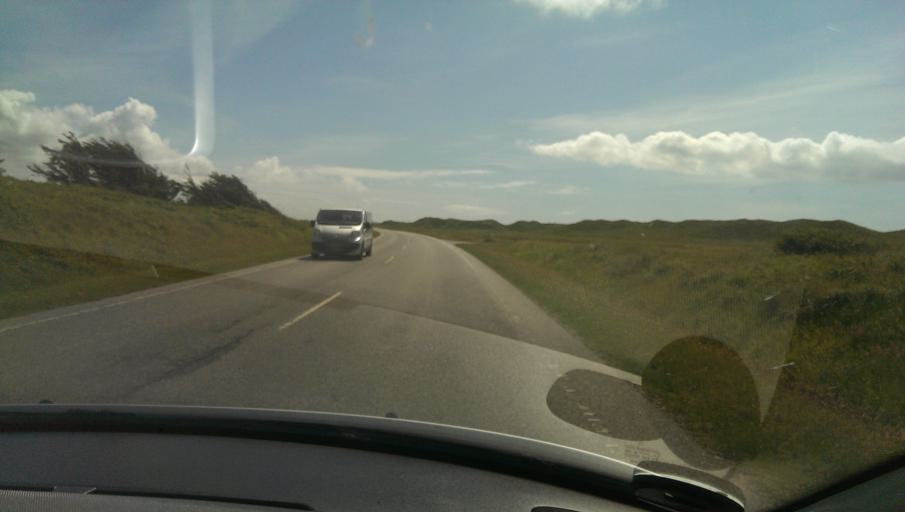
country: DK
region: Central Jutland
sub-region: Ringkobing-Skjern Kommune
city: Ringkobing
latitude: 56.2122
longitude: 8.1349
